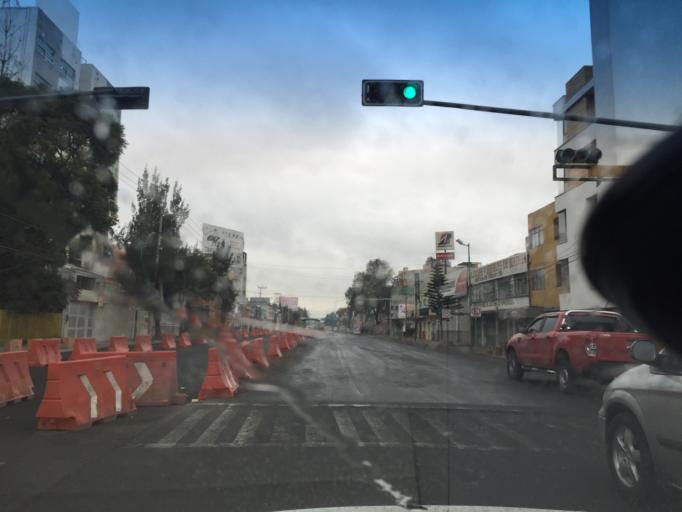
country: MX
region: Mexico
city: Colonia Lindavista
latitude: 19.4926
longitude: -99.1425
